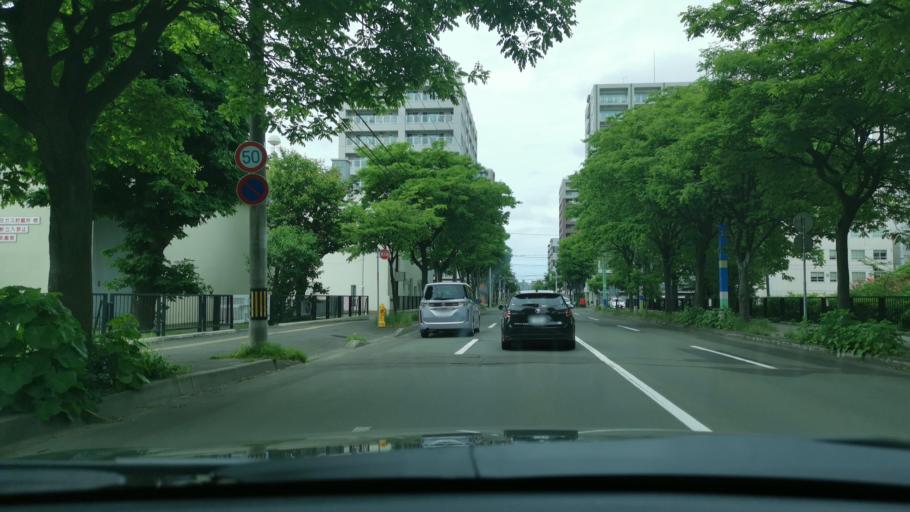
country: JP
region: Hokkaido
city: Sapporo
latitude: 43.0600
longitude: 141.3296
